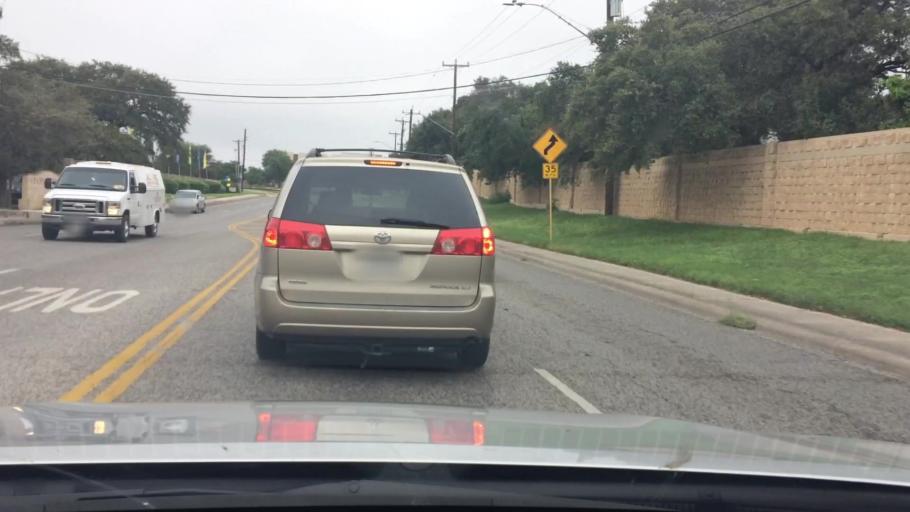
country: US
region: Texas
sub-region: Bexar County
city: Hollywood Park
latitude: 29.5821
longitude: -98.4468
